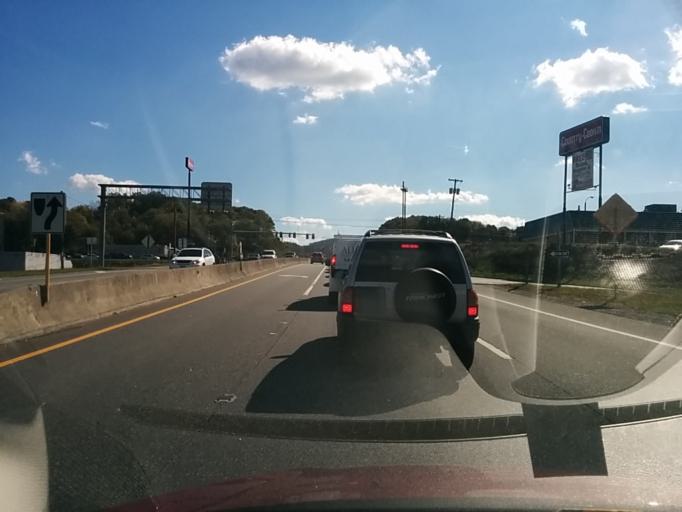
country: US
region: Virginia
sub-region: Botetourt County
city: Cloverdale
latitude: 37.3880
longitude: -79.9042
